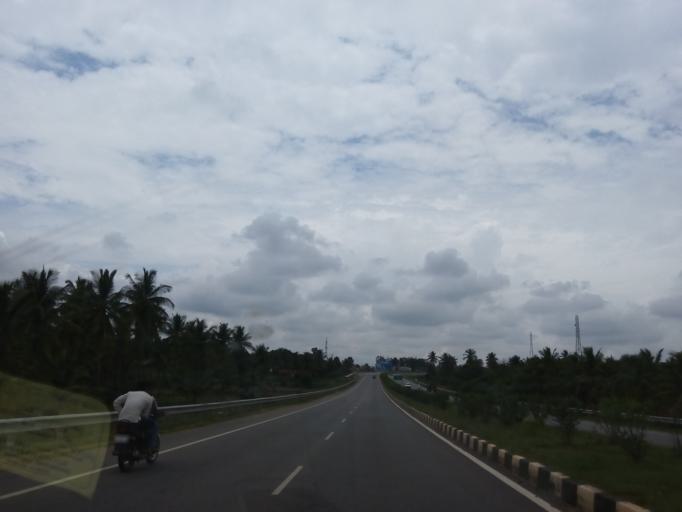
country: IN
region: Karnataka
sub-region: Hassan
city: Channarayapatna
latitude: 12.9752
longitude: 76.2838
